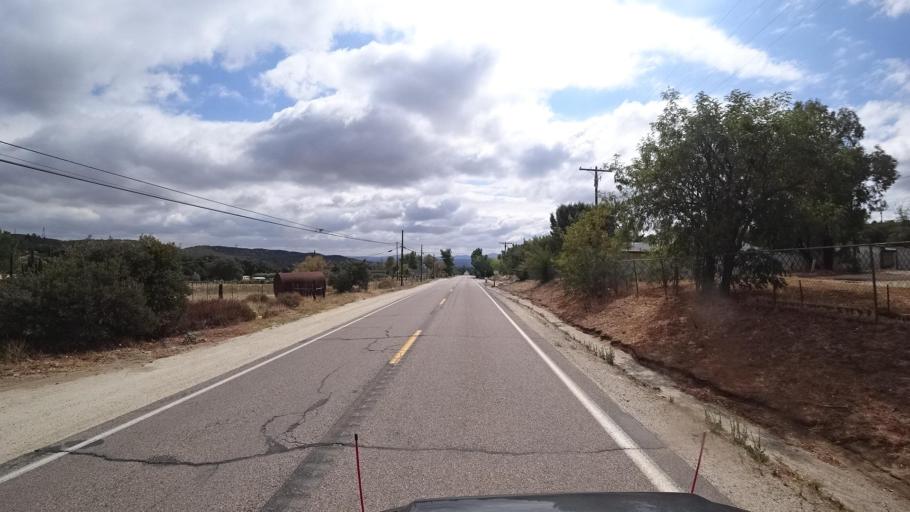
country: US
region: California
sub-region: San Diego County
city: Campo
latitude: 32.6756
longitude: -116.4886
